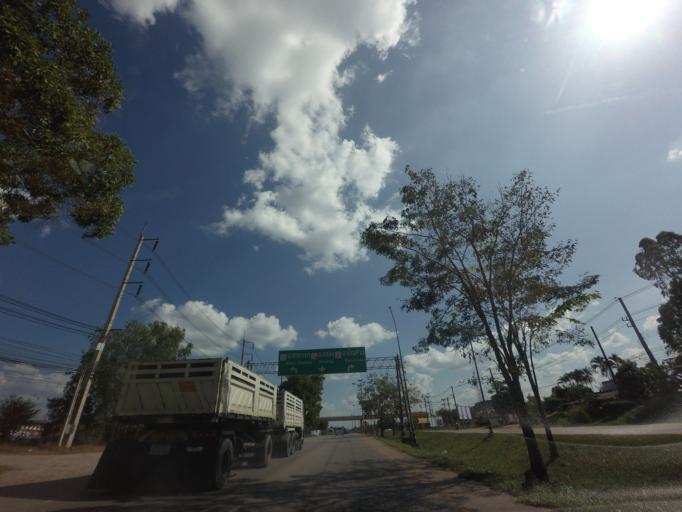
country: TH
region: Rayong
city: Wang Chan
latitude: 12.9391
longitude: 101.5211
